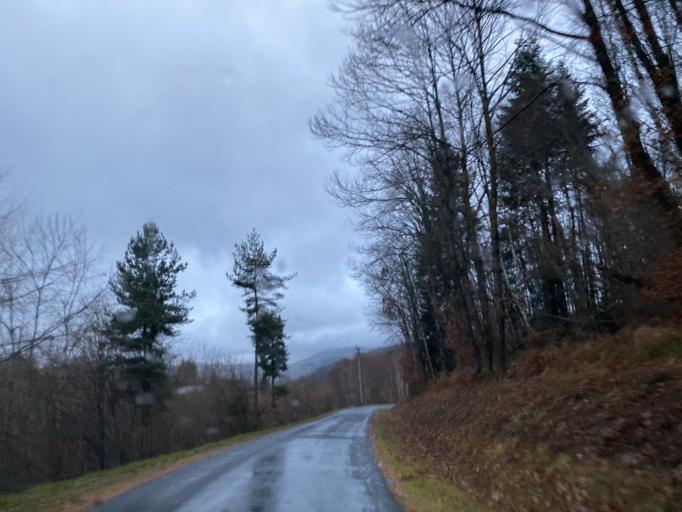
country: FR
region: Auvergne
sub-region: Departement du Puy-de-Dome
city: La Monnerie-le-Montel
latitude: 45.8590
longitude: 3.6145
